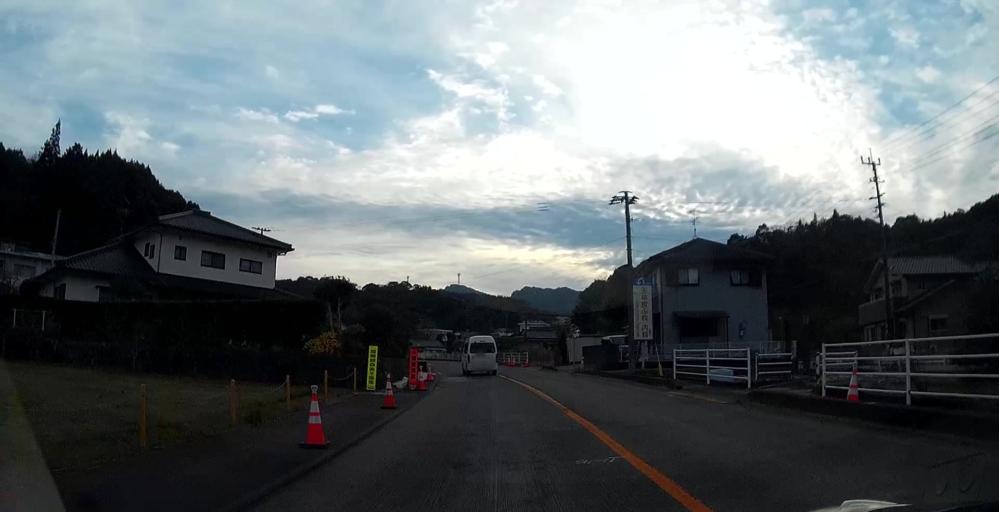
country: JP
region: Kumamoto
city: Yatsushiro
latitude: 32.4995
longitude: 130.4247
